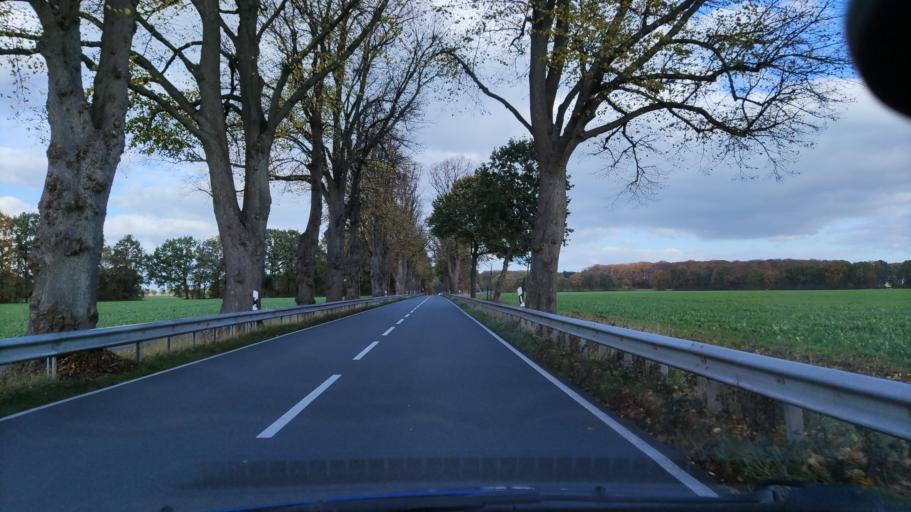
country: DE
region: Lower Saxony
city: Amelinghausen
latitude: 53.1171
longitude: 10.1816
